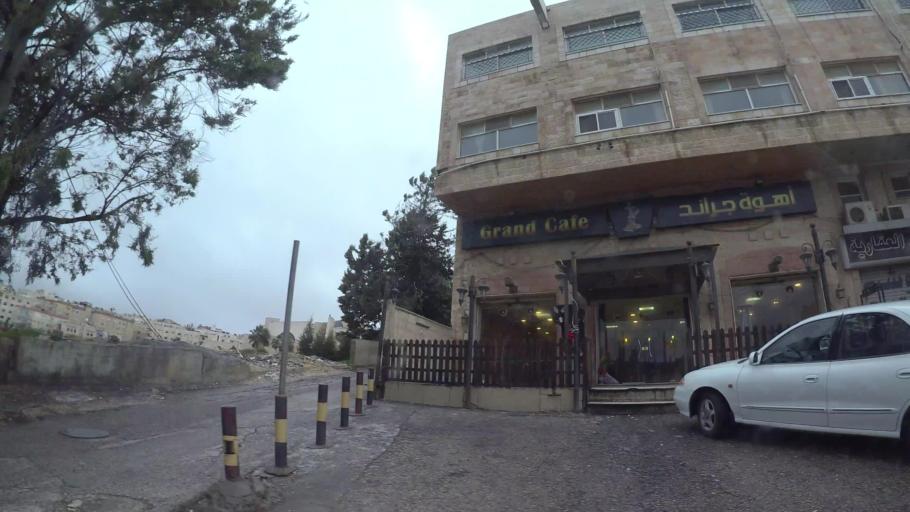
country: JO
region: Amman
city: Al Jubayhah
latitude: 32.0283
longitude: 35.8598
